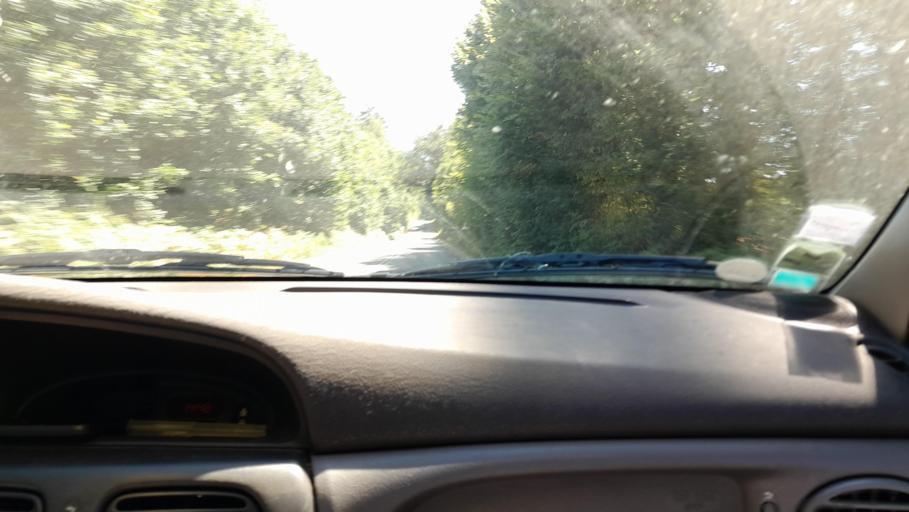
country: FR
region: Pays de la Loire
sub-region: Departement de Maine-et-Loire
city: Pouance
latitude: 47.7130
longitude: -1.1784
